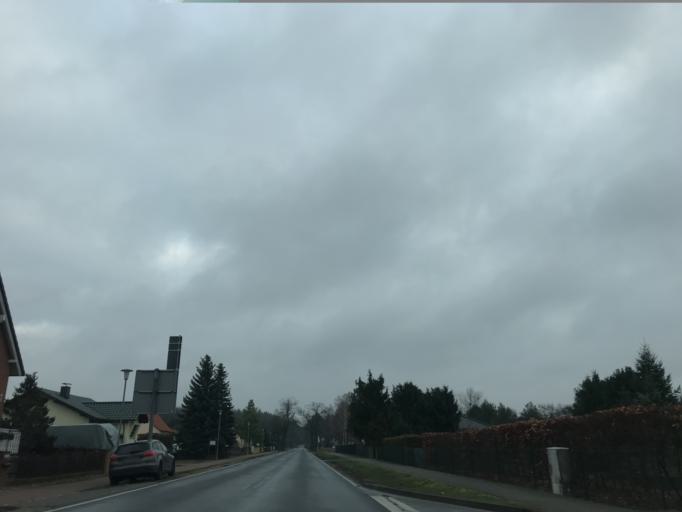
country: DE
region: Brandenburg
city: Nauen
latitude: 52.6879
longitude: 12.9377
